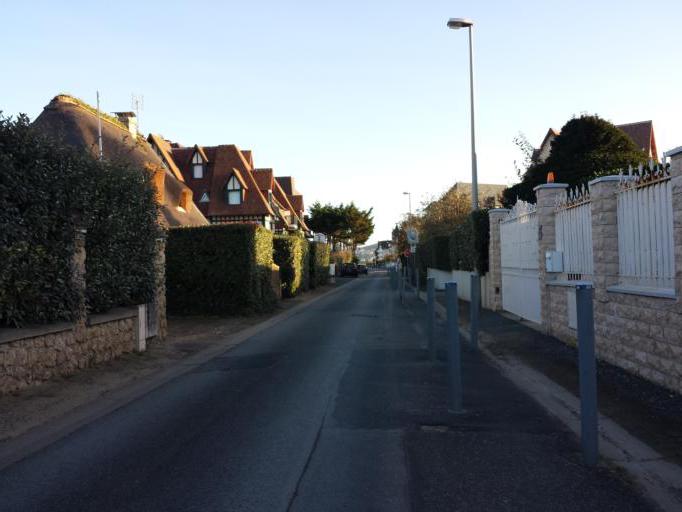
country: FR
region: Lower Normandy
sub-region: Departement du Calvados
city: Deauville
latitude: 49.3516
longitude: 0.0527
